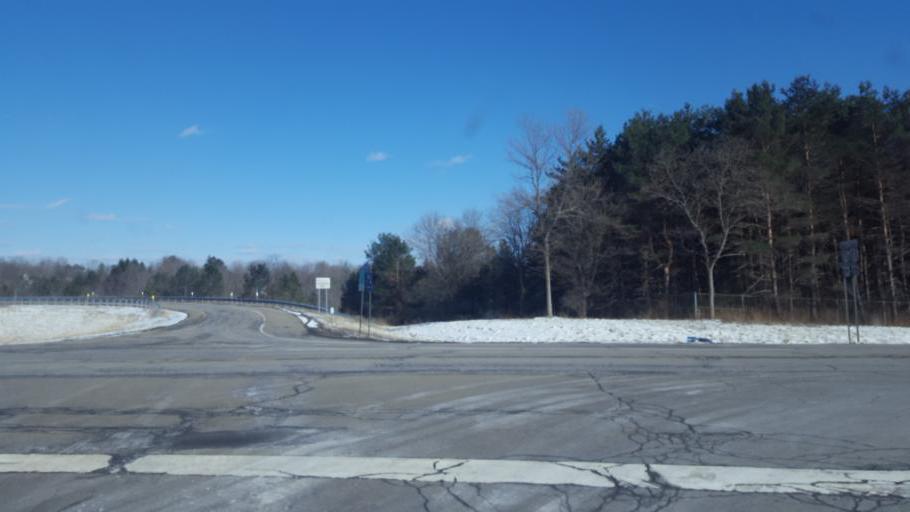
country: US
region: New York
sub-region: Allegany County
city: Friendship
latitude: 42.2091
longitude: -78.1460
